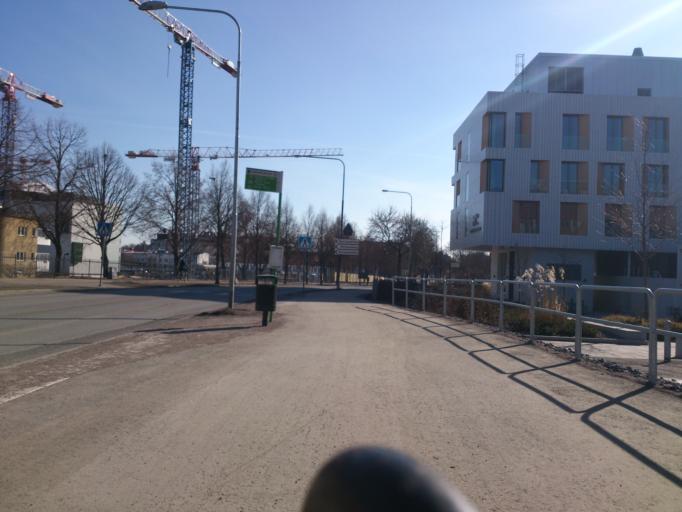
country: SE
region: Uppsala
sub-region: Uppsala Kommun
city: Uppsala
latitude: 59.8491
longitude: 17.6361
